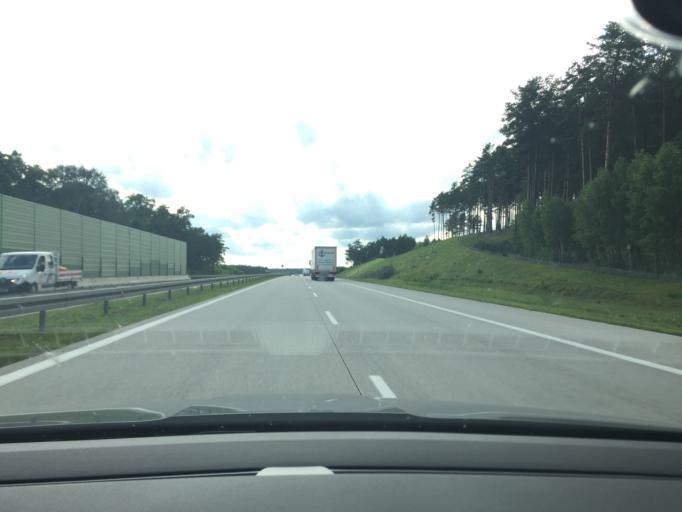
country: PL
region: Lubusz
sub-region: Powiat sulecinski
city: Torzym
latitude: 52.3327
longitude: 15.0117
